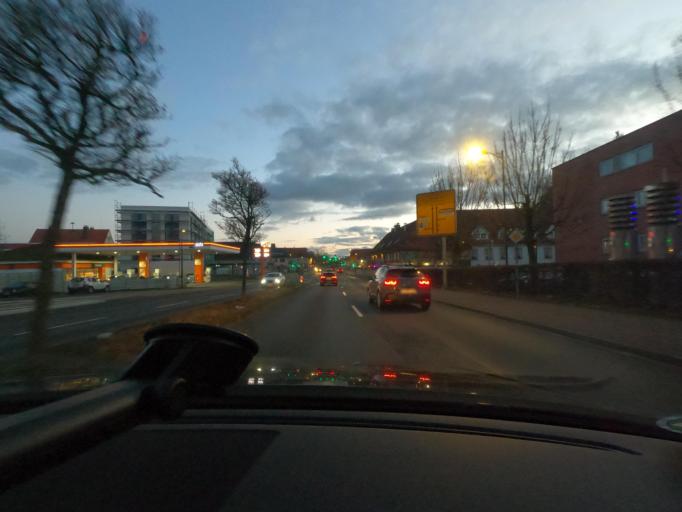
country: DE
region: Lower Saxony
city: Herzberg am Harz
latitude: 51.6570
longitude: 10.3339
